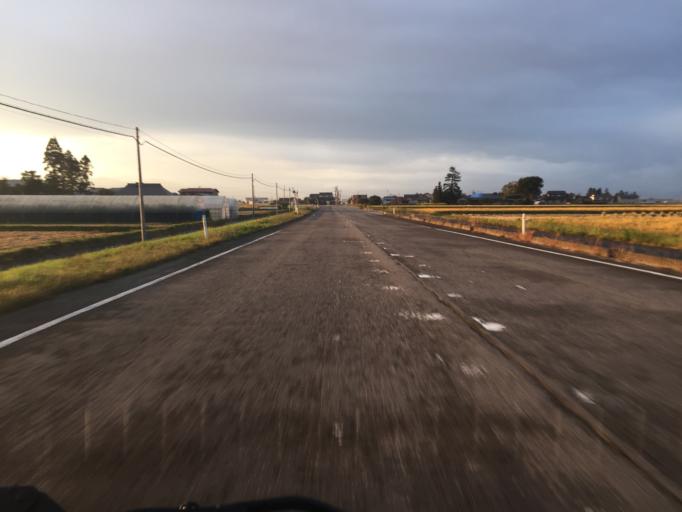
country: JP
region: Fukushima
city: Kitakata
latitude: 37.5637
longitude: 139.8889
